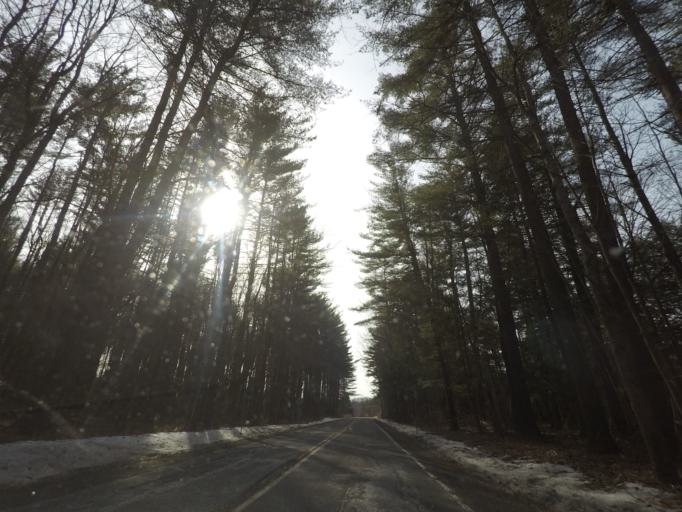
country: US
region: New York
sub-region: Rensselaer County
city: Nassau
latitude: 42.4852
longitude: -73.5611
